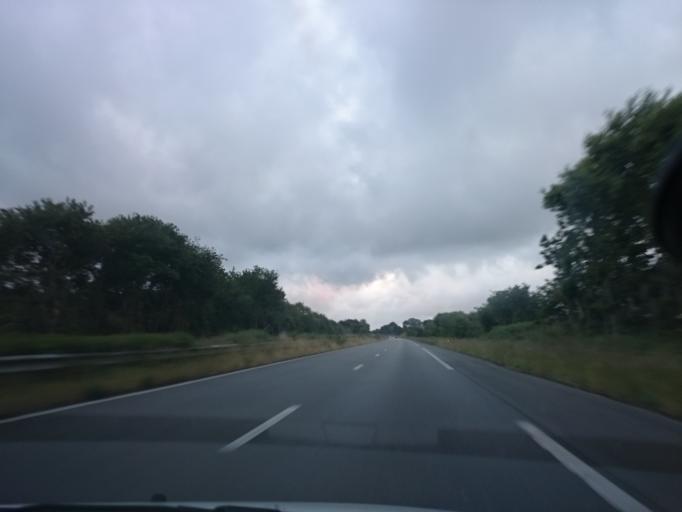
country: FR
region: Brittany
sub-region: Departement du Finistere
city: Le Trevoux
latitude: 47.8759
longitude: -3.6200
